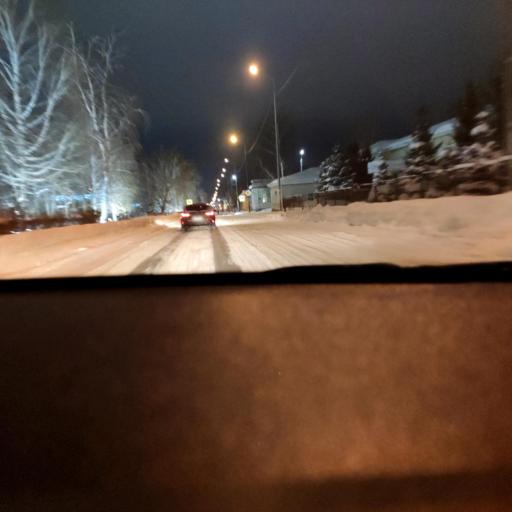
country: RU
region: Tatarstan
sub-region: Chistopol'skiy Rayon
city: Chistopol'
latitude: 55.3653
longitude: 50.6444
